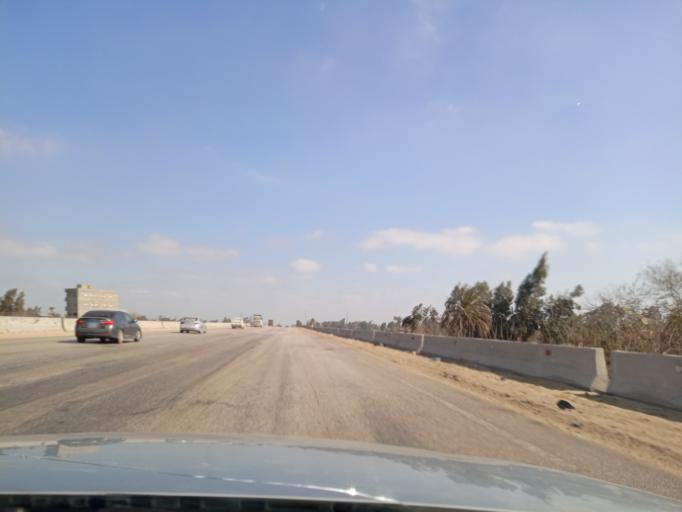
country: EG
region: Muhafazat al Minufiyah
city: Al Bajur
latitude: 30.4308
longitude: 31.0991
